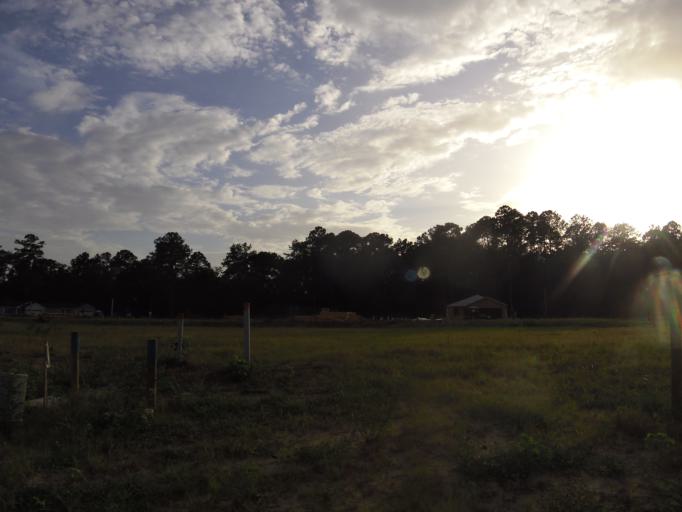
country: US
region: Florida
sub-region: Duval County
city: Jacksonville
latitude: 30.4176
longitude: -81.7348
